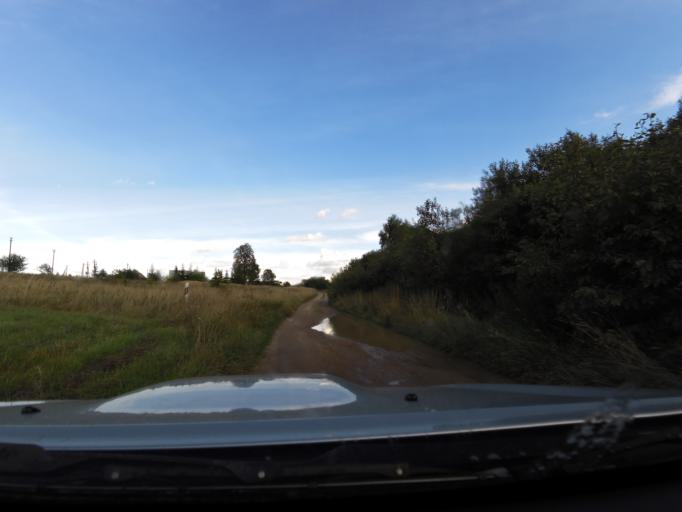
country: LT
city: Lentvaris
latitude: 54.6426
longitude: 24.9933
